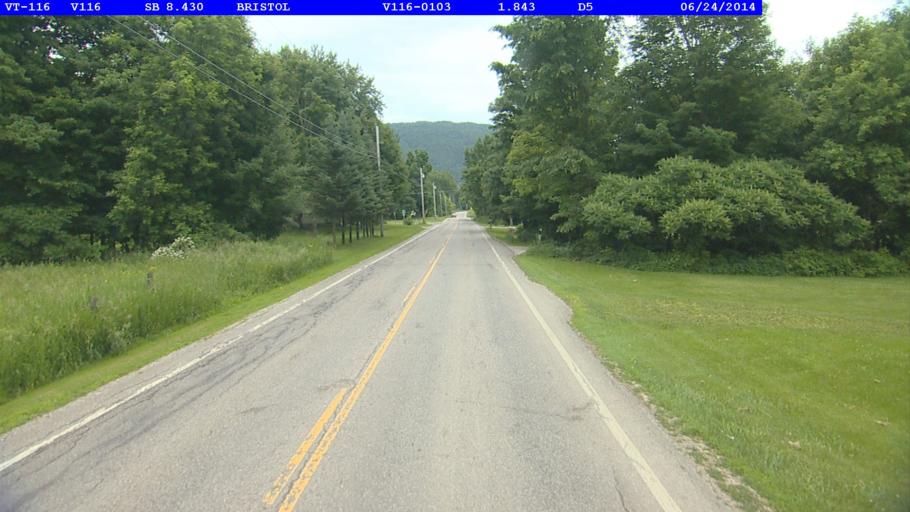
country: US
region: Vermont
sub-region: Addison County
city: Bristol
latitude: 44.0800
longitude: -73.0871
